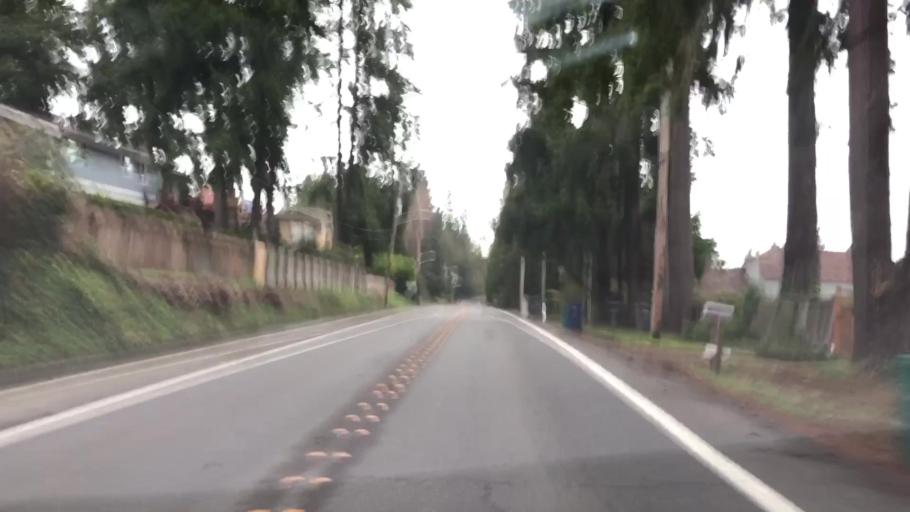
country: US
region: Washington
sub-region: King County
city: Sammamish
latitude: 47.6396
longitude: -122.0988
